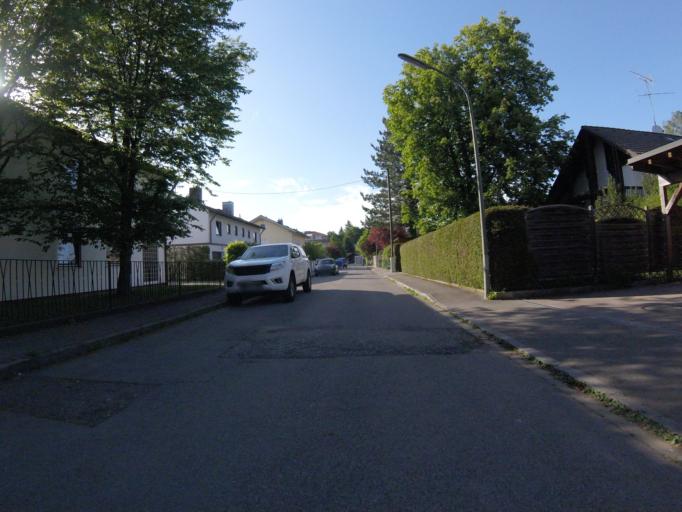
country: DE
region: Bavaria
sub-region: Upper Bavaria
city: Ottobrunn
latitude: 48.0663
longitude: 11.6690
